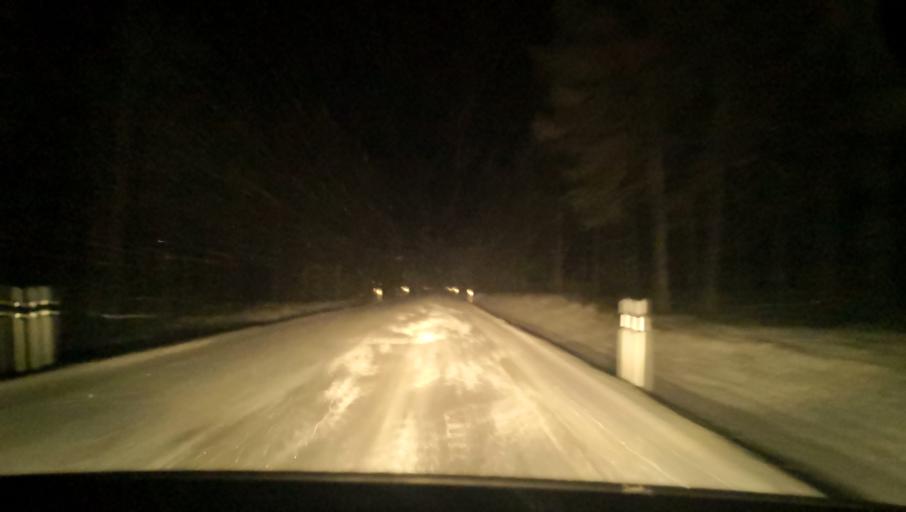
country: SE
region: Uppsala
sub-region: Heby Kommun
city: Tarnsjo
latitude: 60.1234
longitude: 16.8864
